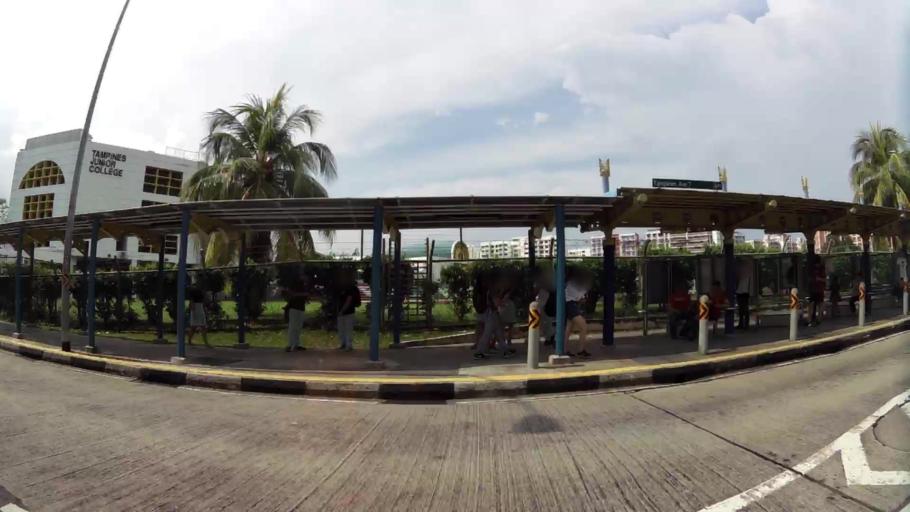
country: SG
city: Singapore
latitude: 1.3567
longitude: 103.9574
